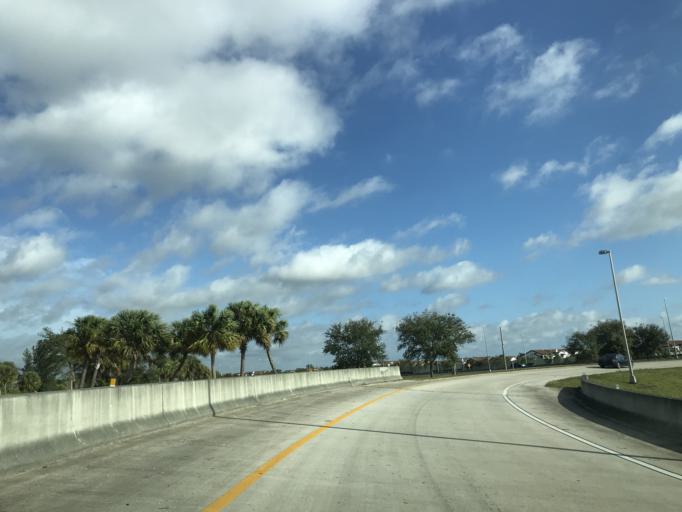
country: US
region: Florida
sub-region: Palm Beach County
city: Villages of Oriole
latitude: 26.4571
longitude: -80.1762
